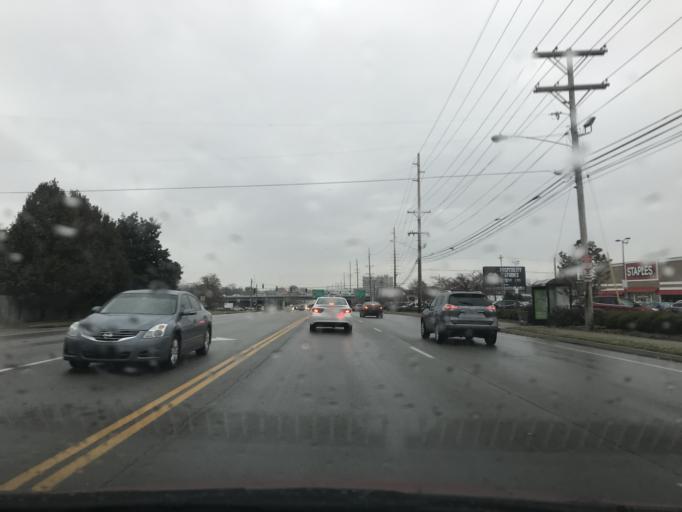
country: US
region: Kentucky
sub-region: Jefferson County
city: West Buechel
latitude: 38.2139
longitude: -85.6734
